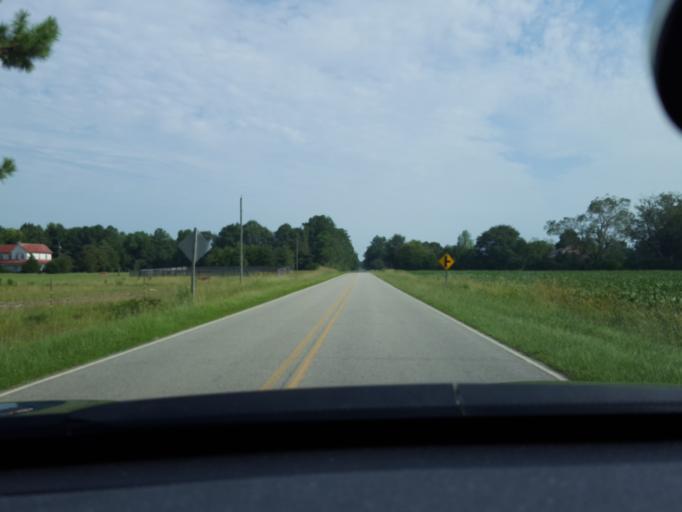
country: US
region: North Carolina
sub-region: Washington County
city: Plymouth
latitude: 35.8799
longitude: -76.7116
